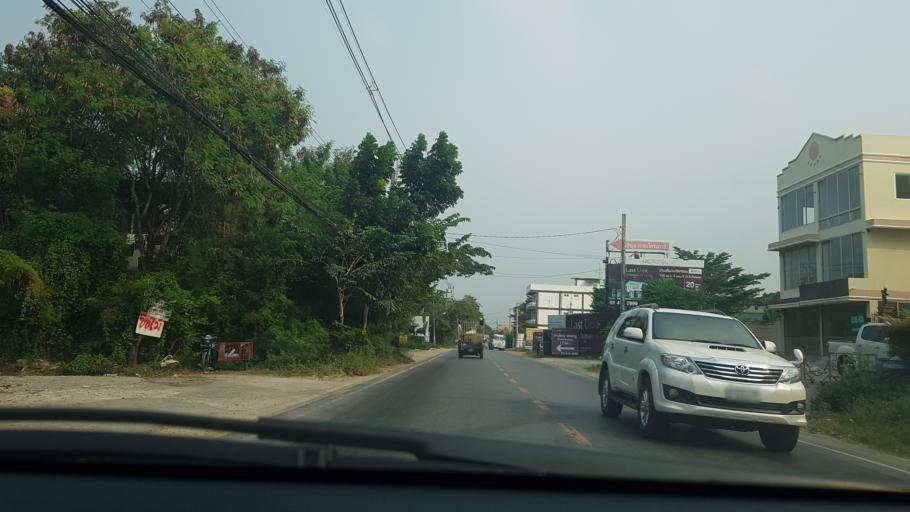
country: TH
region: Bangkok
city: Phasi Charoen
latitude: 13.7559
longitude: 100.3985
